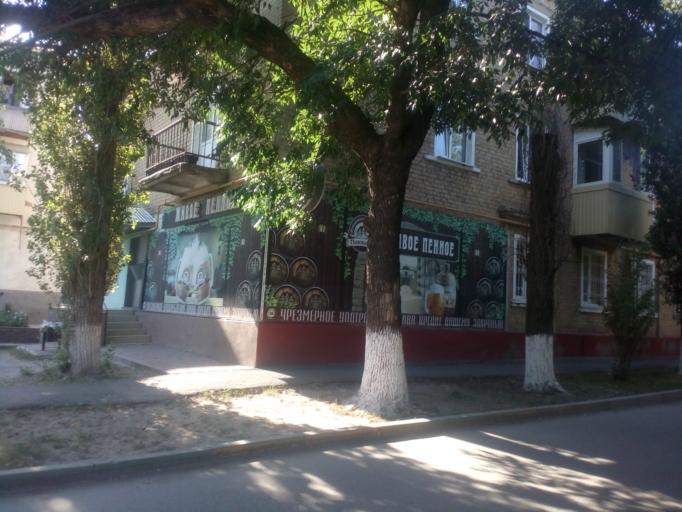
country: RU
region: Rostov
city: Sholokhovskiy
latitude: 48.2823
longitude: 41.0503
